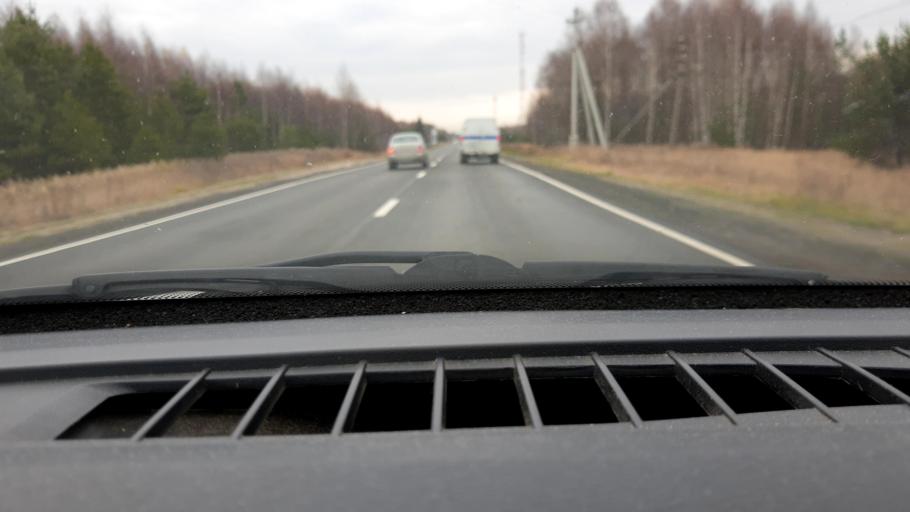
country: RU
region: Nizjnij Novgorod
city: Novaya Balakhna
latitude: 56.6025
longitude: 43.6275
